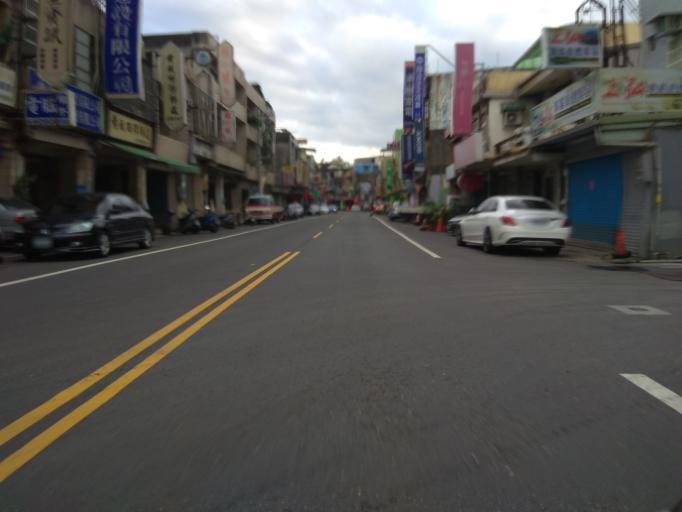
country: TW
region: Taiwan
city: Daxi
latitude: 24.8678
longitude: 121.2137
